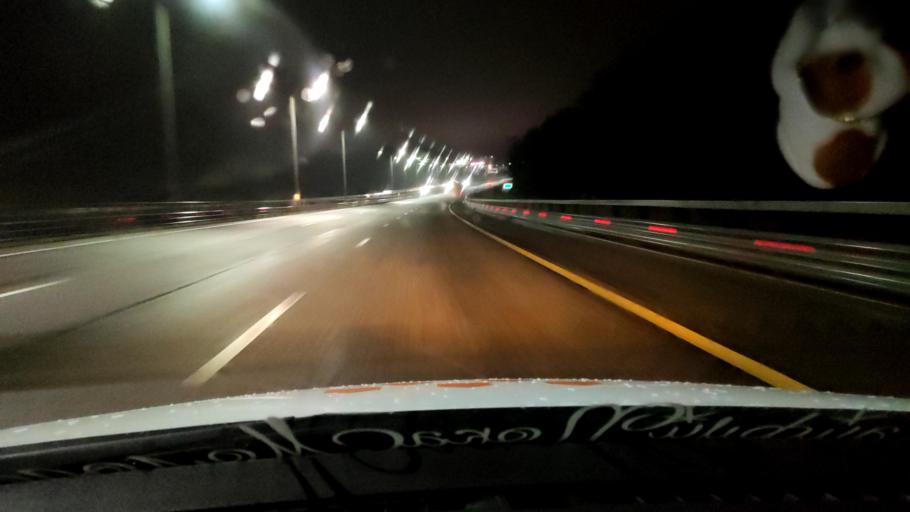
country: RU
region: Voronezj
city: Ramon'
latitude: 51.8305
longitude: 39.2420
